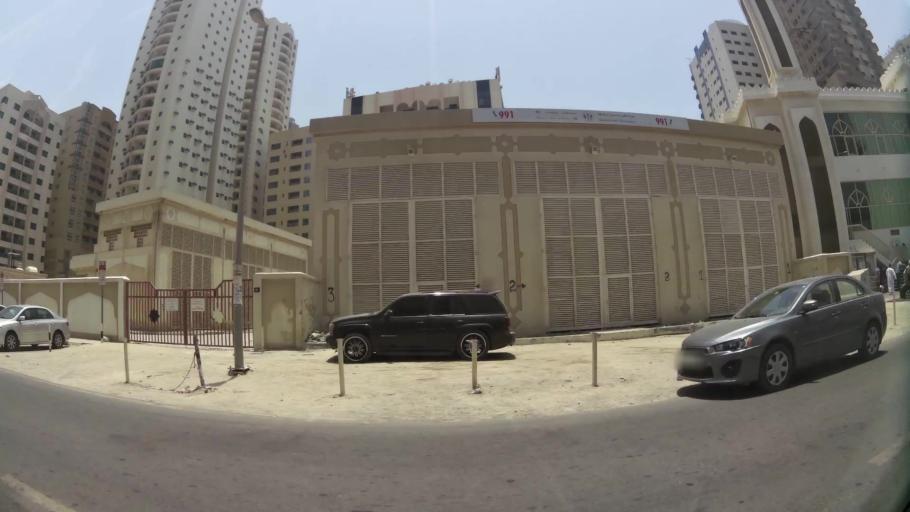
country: AE
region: Ash Shariqah
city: Sharjah
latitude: 25.3272
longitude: 55.3777
